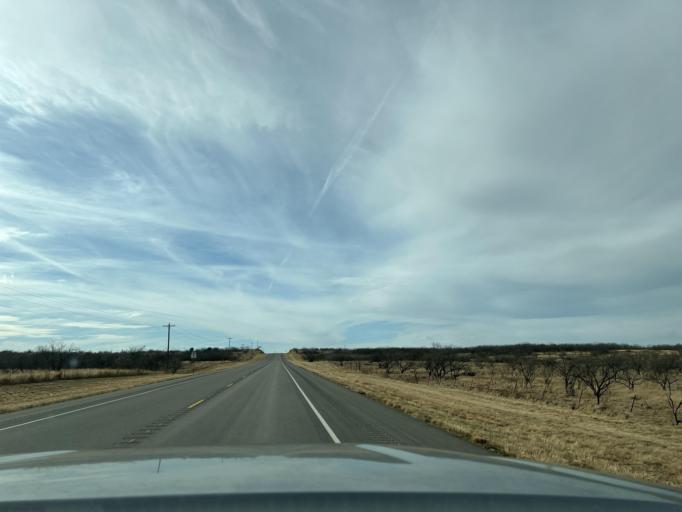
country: US
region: Texas
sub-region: Jones County
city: Anson
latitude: 32.7508
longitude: -99.7407
